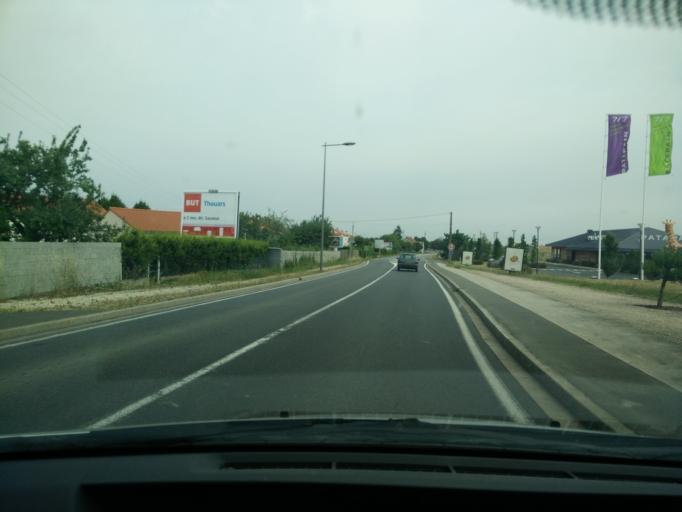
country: FR
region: Poitou-Charentes
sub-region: Departement des Deux-Sevres
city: Thouars
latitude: 46.9797
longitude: -0.1989
